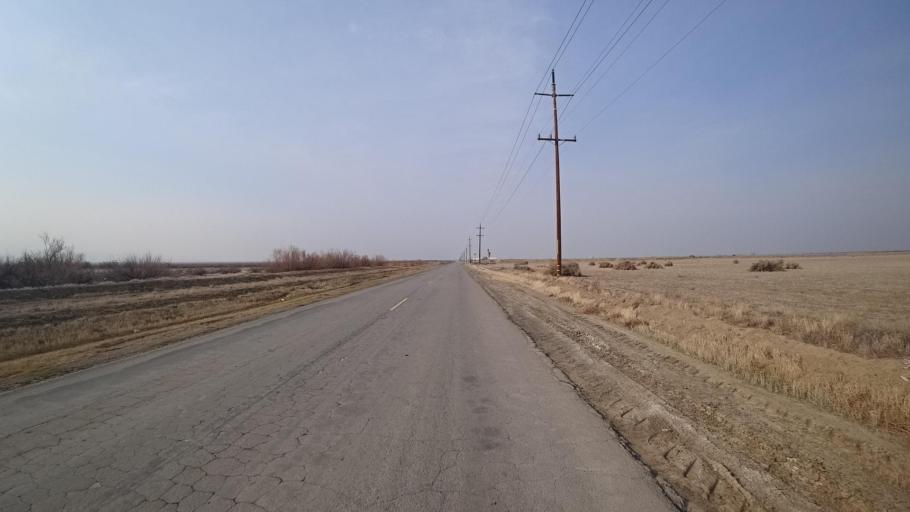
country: US
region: California
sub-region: Kern County
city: Greenfield
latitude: 35.0949
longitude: -119.0623
